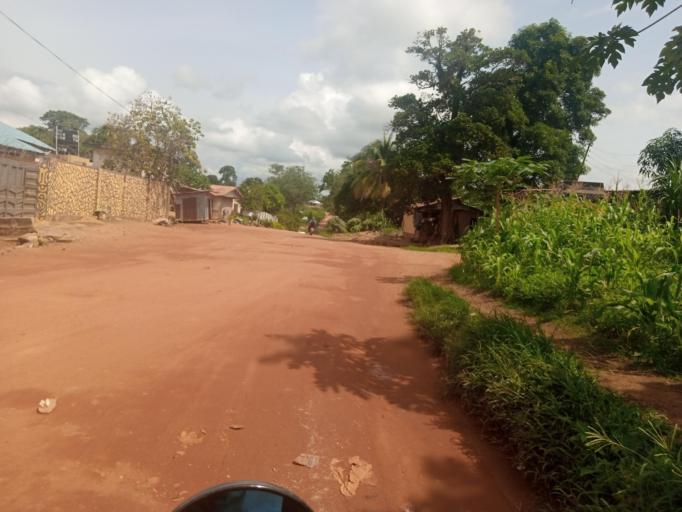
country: SL
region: Southern Province
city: Bo
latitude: 7.9671
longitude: -11.7445
